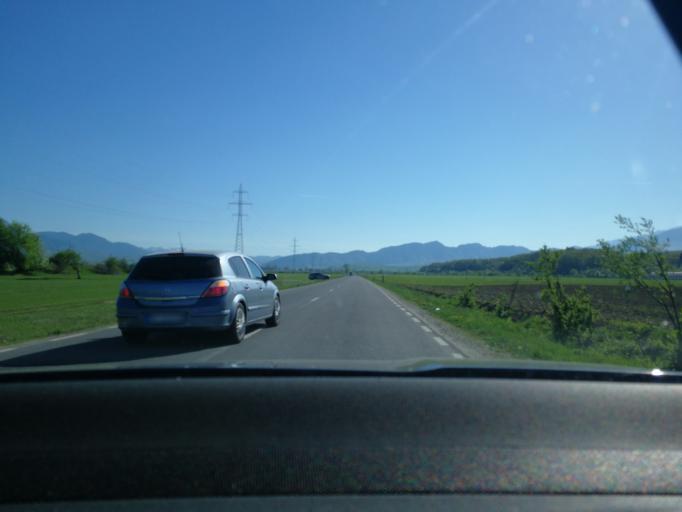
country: RO
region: Brasov
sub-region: Oras Rasnov
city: Rasnov
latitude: 45.5944
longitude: 25.4170
